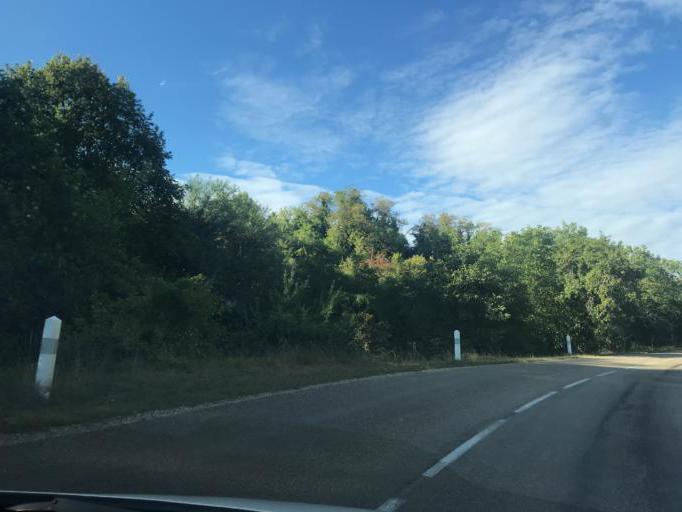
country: FR
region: Bourgogne
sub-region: Departement de l'Yonne
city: Fontenailles
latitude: 47.5501
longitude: 3.4261
